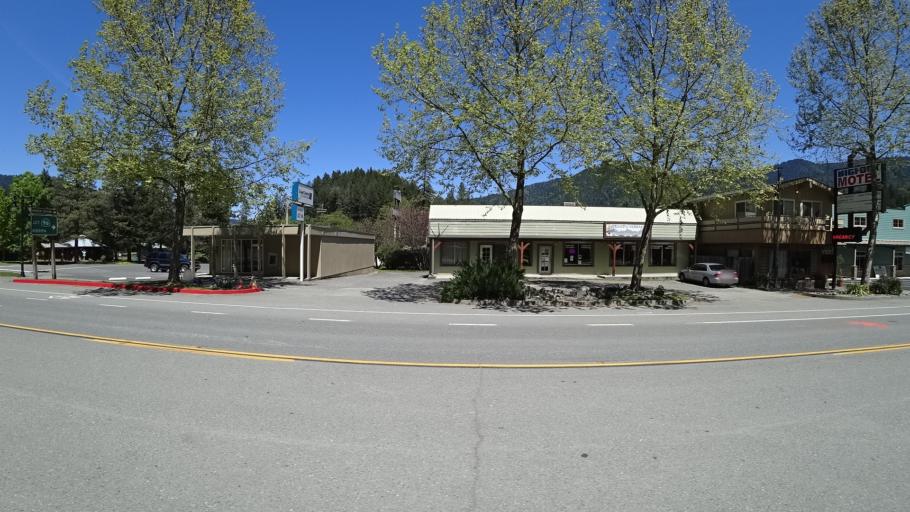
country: US
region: California
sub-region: Humboldt County
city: Willow Creek
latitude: 40.9392
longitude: -123.6310
